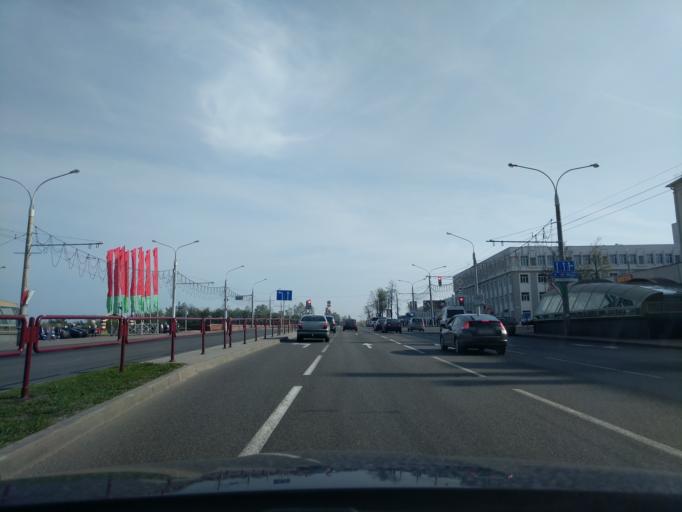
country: BY
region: Minsk
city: Minsk
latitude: 53.8604
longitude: 27.5720
